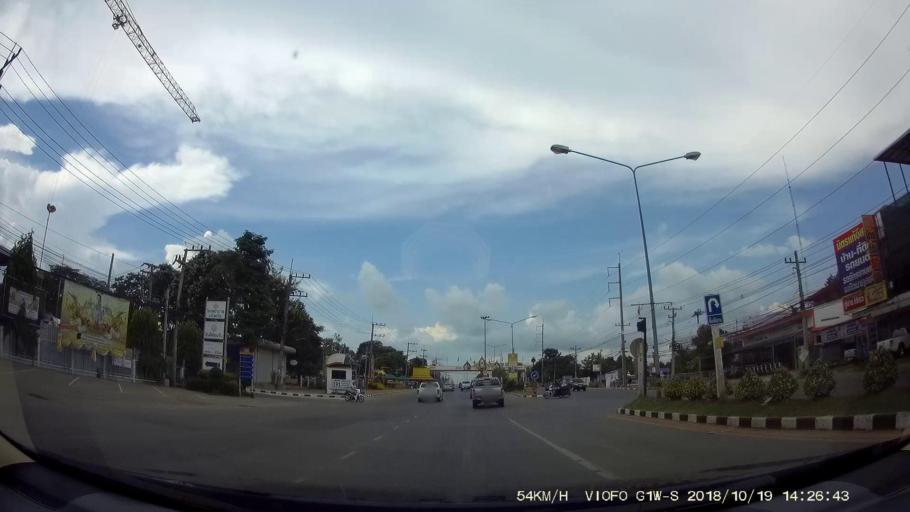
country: TH
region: Chaiyaphum
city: Kaeng Khro
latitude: 16.1083
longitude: 102.2591
